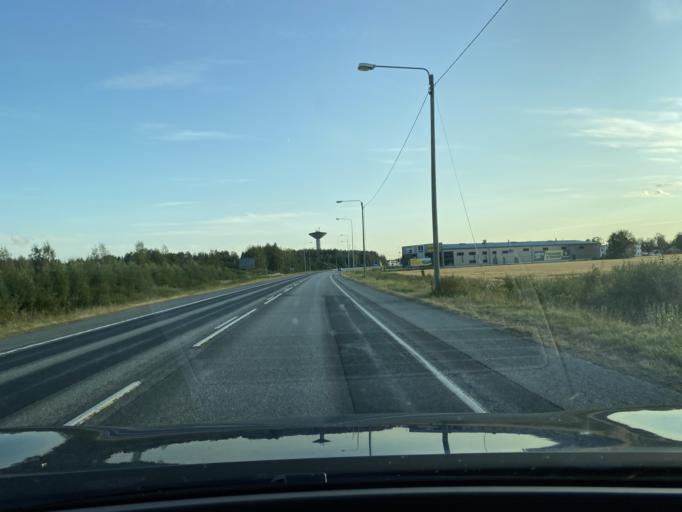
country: FI
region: Southern Ostrobothnia
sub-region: Seinaejoki
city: Nurmo
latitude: 62.8122
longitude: 22.8932
